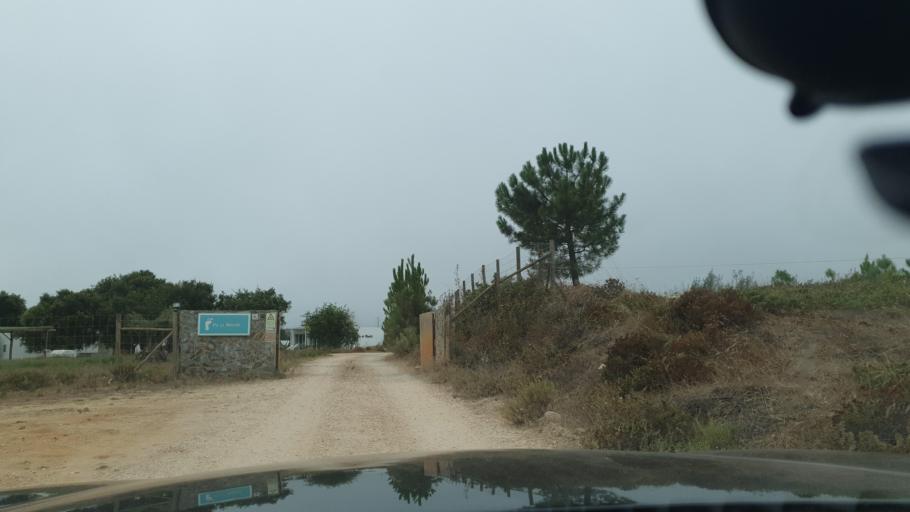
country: PT
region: Beja
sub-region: Odemira
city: Sao Teotonio
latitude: 37.4944
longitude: -8.6862
